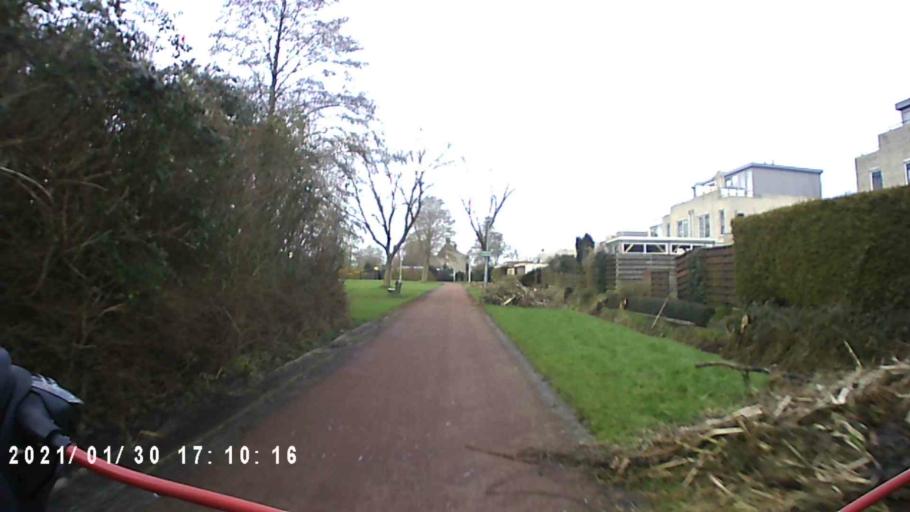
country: NL
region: Groningen
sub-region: Gemeente Leek
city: Leek
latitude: 53.1674
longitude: 6.3641
